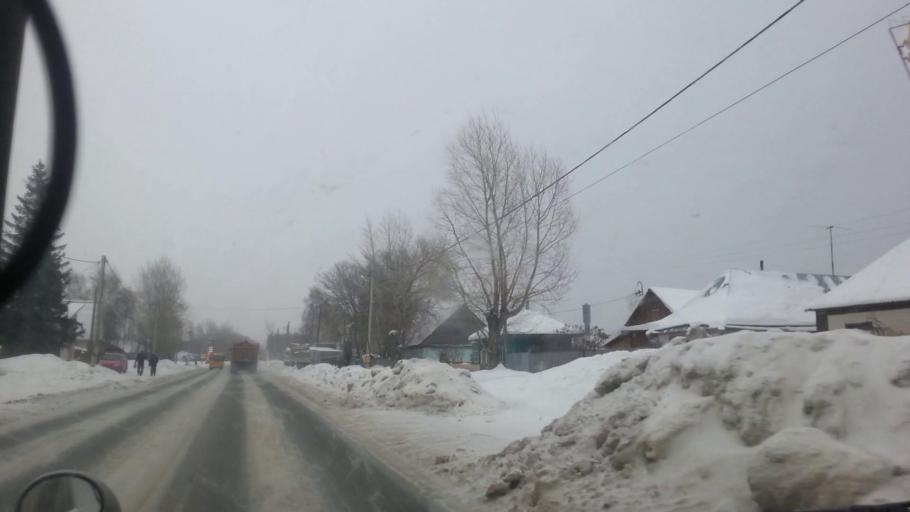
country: RU
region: Altai Krai
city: Vlasikha
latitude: 53.2986
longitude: 83.5887
